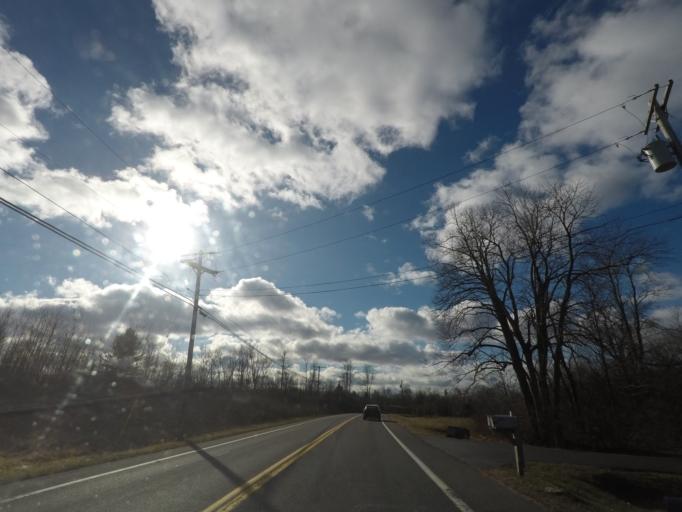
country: US
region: New York
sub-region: Saratoga County
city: Country Knolls
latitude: 42.9210
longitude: -73.8592
